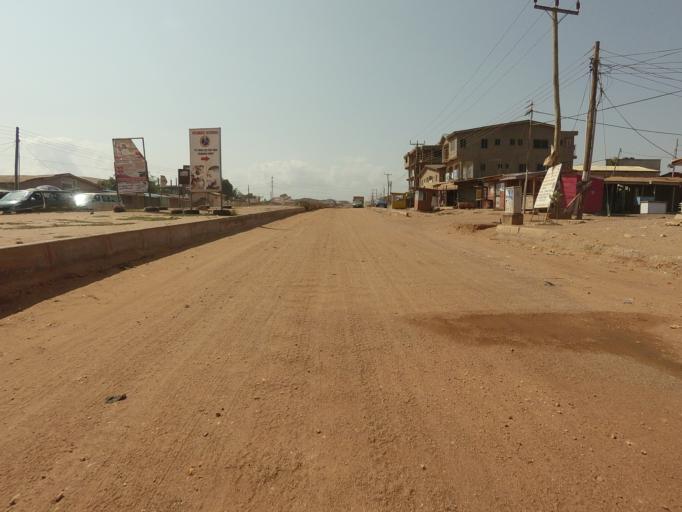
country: GH
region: Greater Accra
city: Teshi Old Town
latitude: 5.6128
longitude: -0.1240
